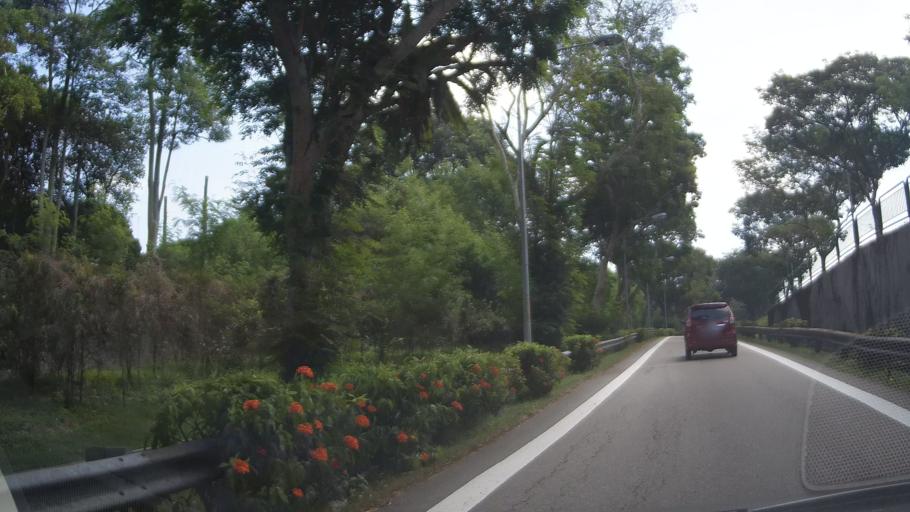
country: MY
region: Johor
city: Johor Bahru
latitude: 1.4231
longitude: 103.7728
